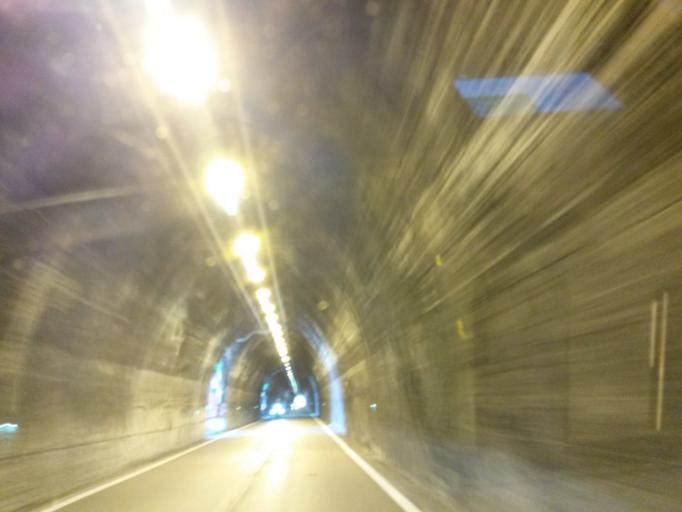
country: IT
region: Lombardy
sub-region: Provincia di Brescia
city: Gargnano
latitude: 45.7080
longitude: 10.6908
